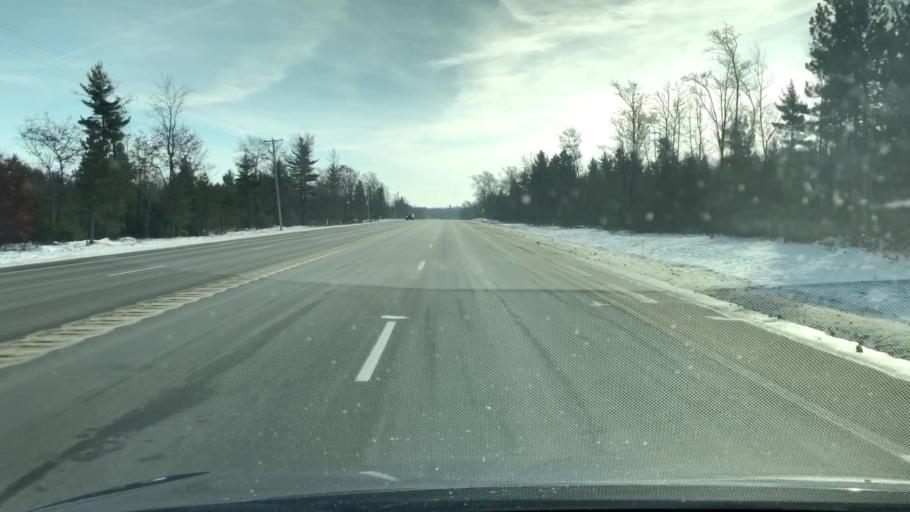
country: US
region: Michigan
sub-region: Kalkaska County
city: Kalkaska
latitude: 44.7525
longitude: -85.2314
